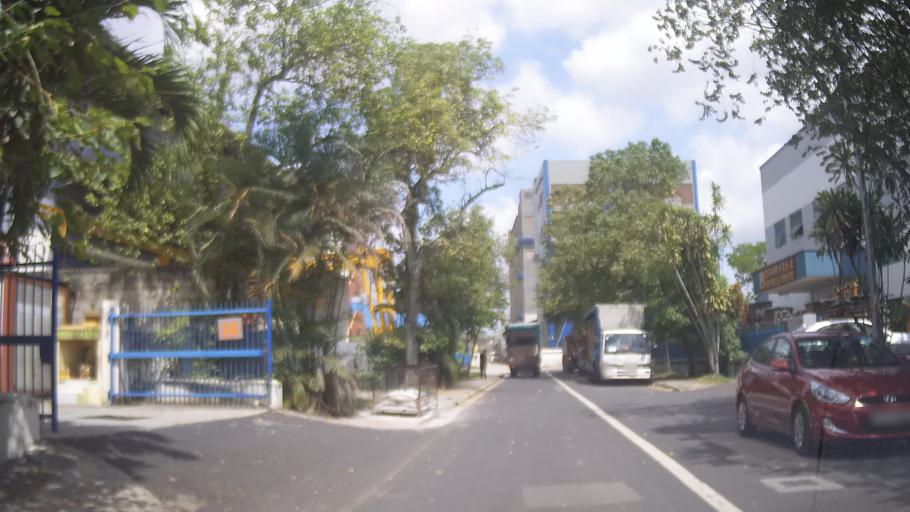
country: MY
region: Johor
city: Johor Bahru
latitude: 1.4286
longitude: 103.7506
